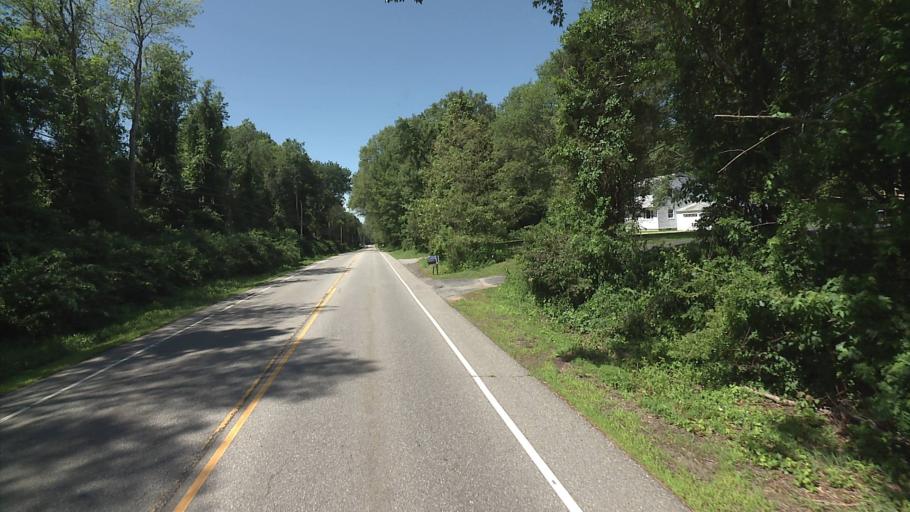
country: US
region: Connecticut
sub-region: New London County
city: Colchester
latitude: 41.5539
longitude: -72.3825
